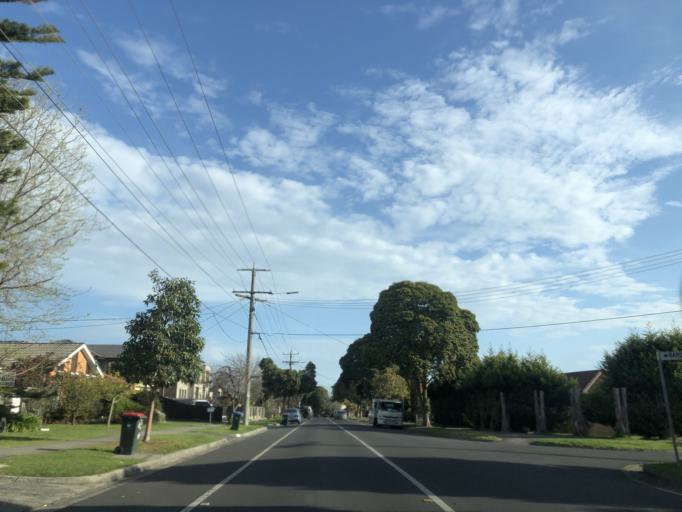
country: AU
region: Victoria
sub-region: Monash
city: Notting Hill
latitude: -37.8976
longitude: 145.1582
